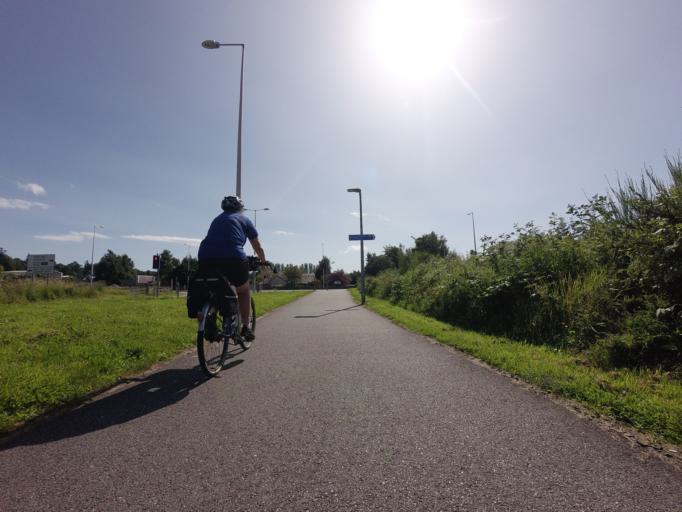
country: GB
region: Scotland
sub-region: Highland
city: Inverness
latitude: 57.4714
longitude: -4.1790
